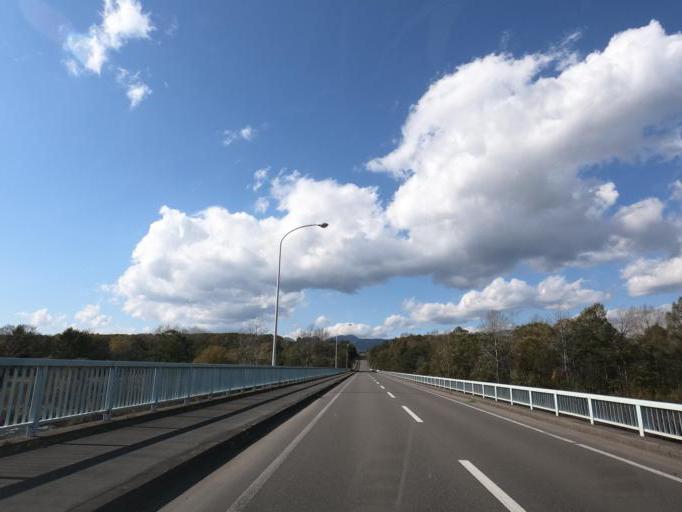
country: JP
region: Hokkaido
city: Otofuke
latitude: 43.2380
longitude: 143.2726
